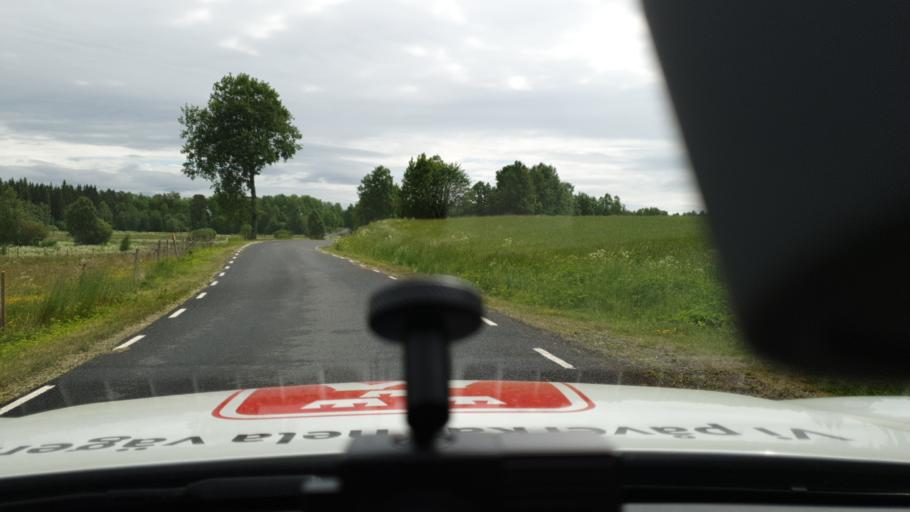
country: SE
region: Joenkoeping
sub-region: Mullsjo Kommun
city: Mullsjoe
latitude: 57.9921
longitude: 13.7396
